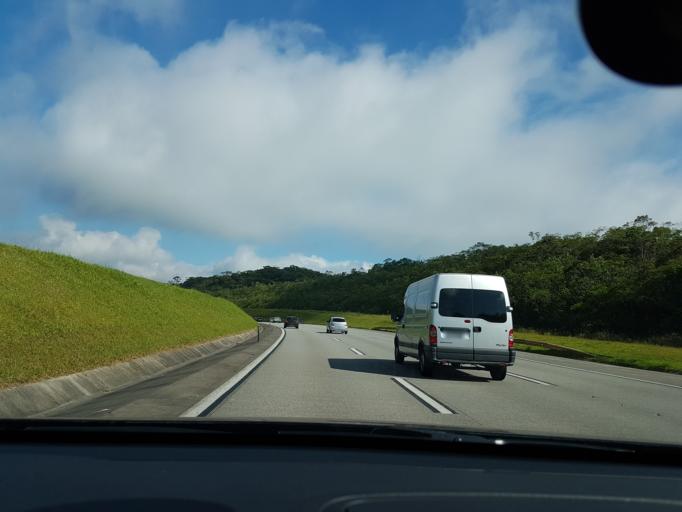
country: BR
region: Sao Paulo
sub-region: Cubatao
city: Cubatao
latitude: -23.9260
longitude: -46.5543
